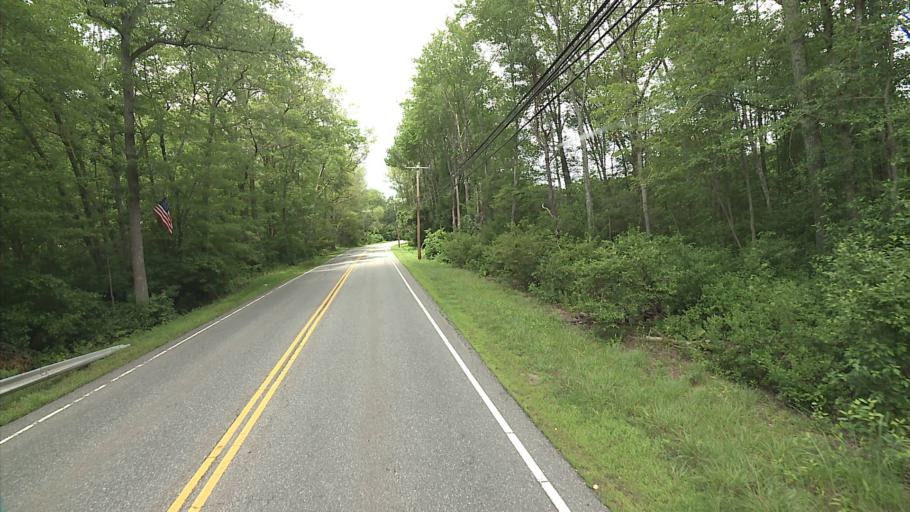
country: US
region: Connecticut
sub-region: Middlesex County
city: Deep River Center
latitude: 41.3773
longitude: -72.4555
